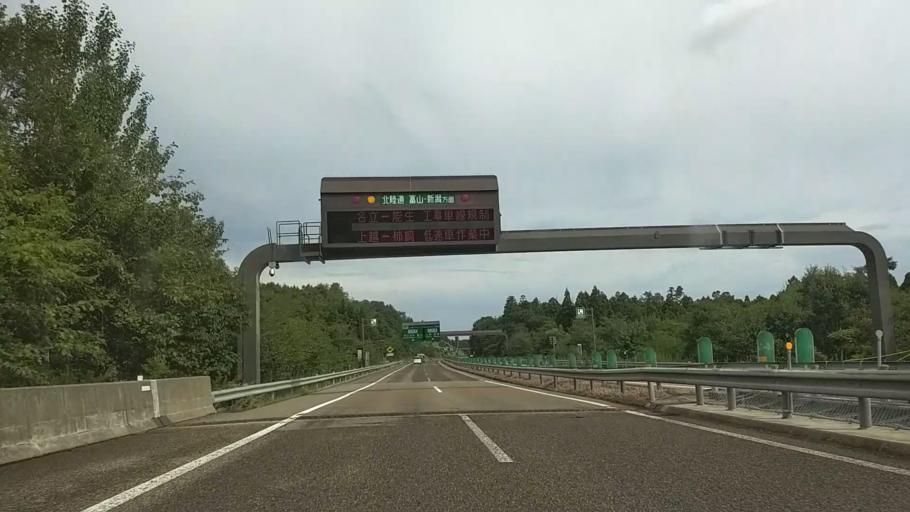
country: JP
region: Niigata
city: Joetsu
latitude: 37.1304
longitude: 138.2126
